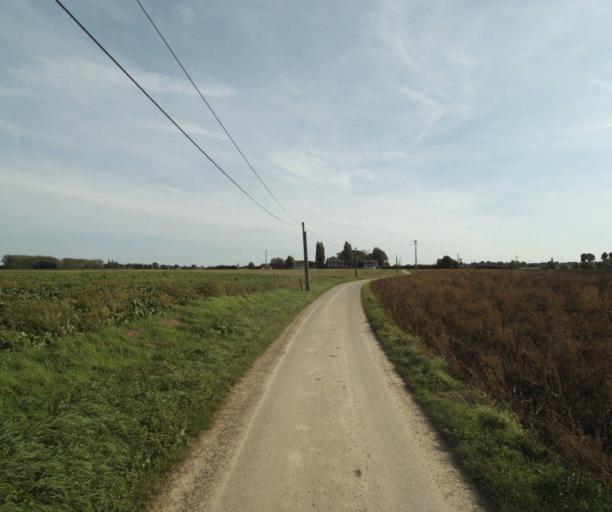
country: FR
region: Nord-Pas-de-Calais
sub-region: Departement du Nord
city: Fournes-en-Weppes
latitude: 50.5998
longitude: 2.8874
